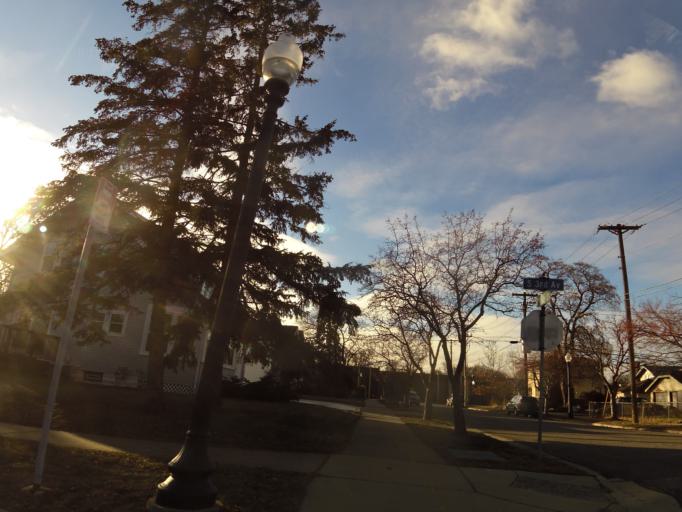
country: US
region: Minnesota
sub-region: Hennepin County
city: Richfield
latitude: 44.9160
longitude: -93.2729
